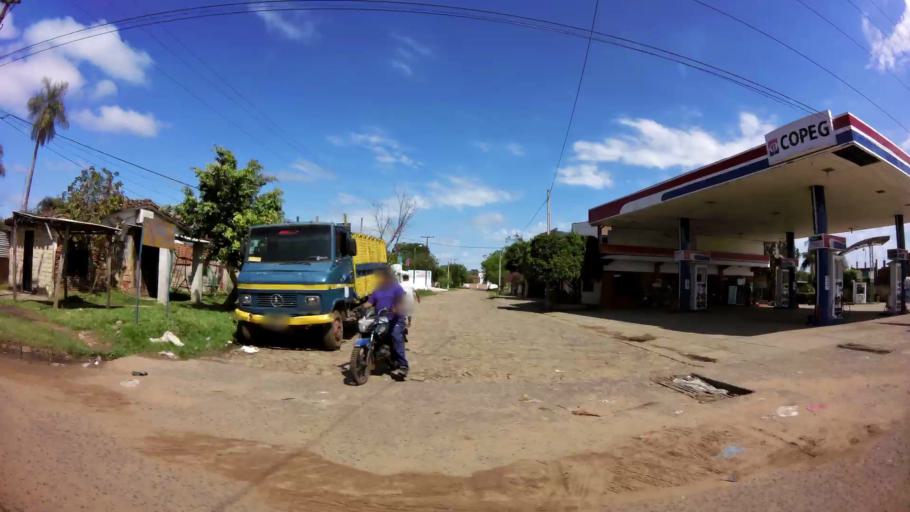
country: PY
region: Central
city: Limpio
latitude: -25.2539
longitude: -57.4886
